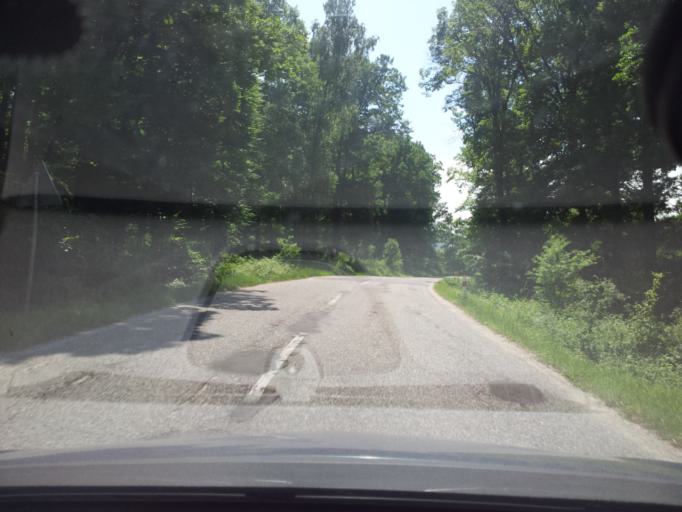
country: SK
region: Nitriansky
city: Partizanske
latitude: 48.5494
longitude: 18.4385
